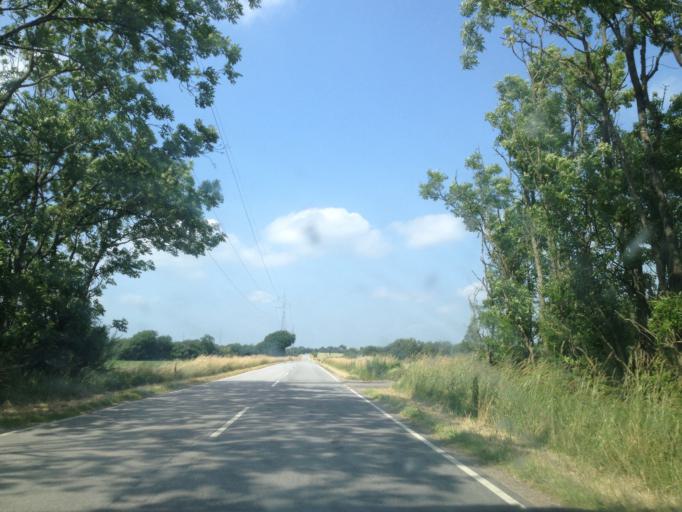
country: DK
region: South Denmark
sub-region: Kolding Kommune
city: Vamdrup
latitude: 55.3661
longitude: 9.2826
